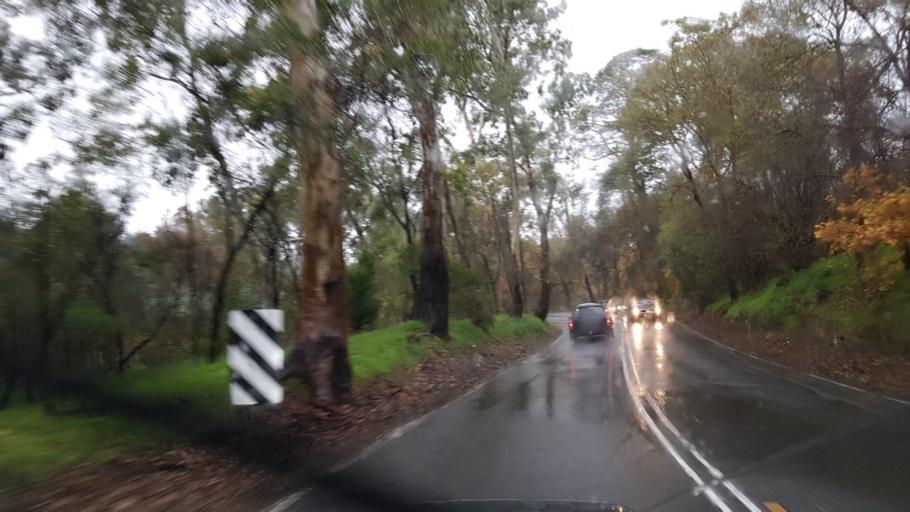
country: AU
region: South Australia
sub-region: Mitcham
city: Blackwood
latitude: -35.0300
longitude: 138.6254
